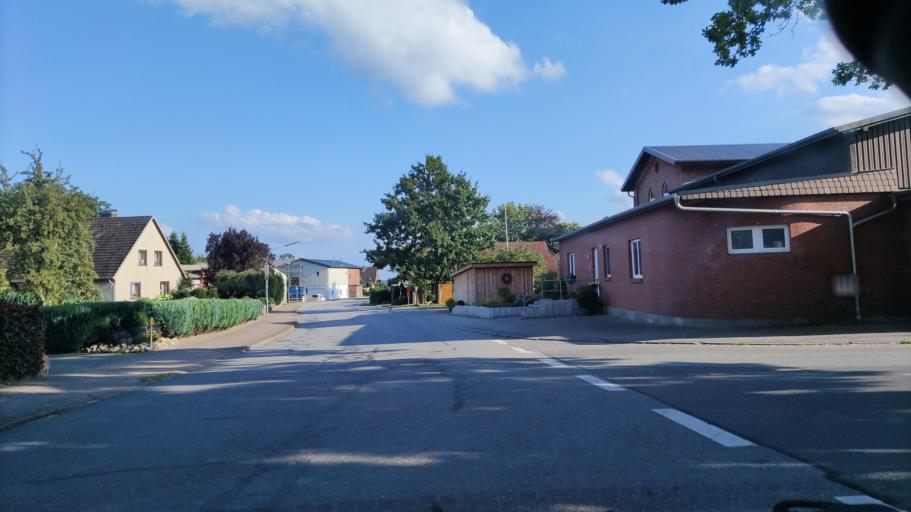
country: DE
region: Schleswig-Holstein
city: Sarlhusen
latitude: 54.0230
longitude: 9.7932
